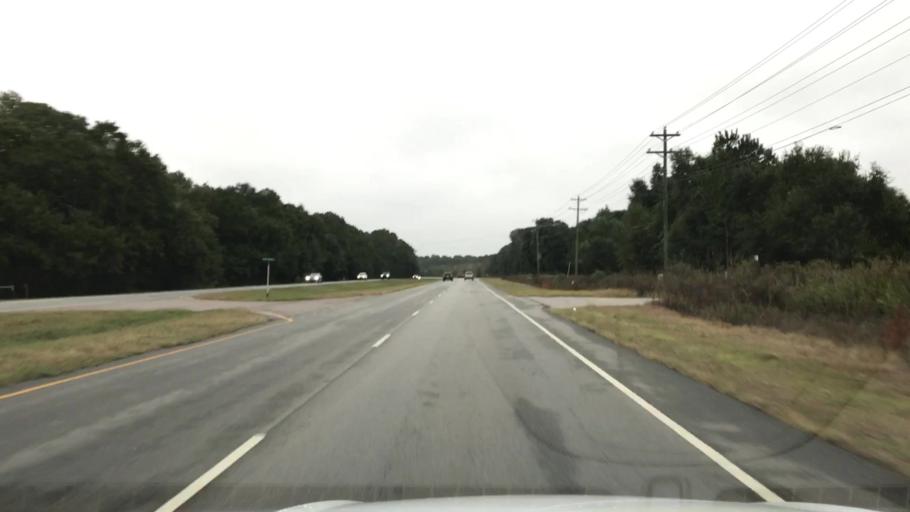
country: US
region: South Carolina
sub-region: Charleston County
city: Isle of Palms
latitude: 32.9139
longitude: -79.7201
